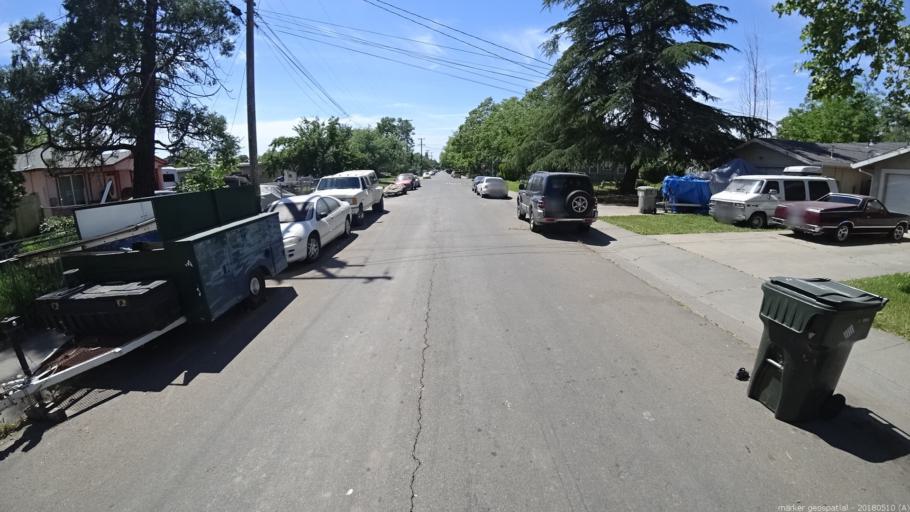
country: US
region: California
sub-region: Sacramento County
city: Rio Linda
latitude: 38.6358
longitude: -121.4496
